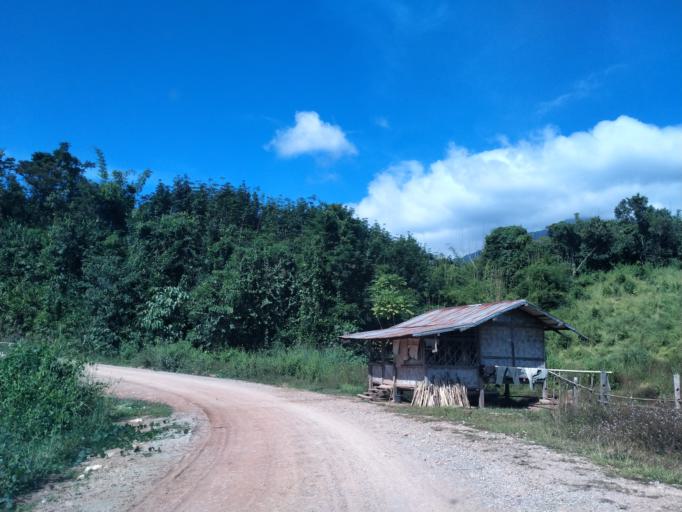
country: TH
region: Changwat Bueng Kan
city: Pak Khat
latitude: 18.6401
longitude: 103.0056
